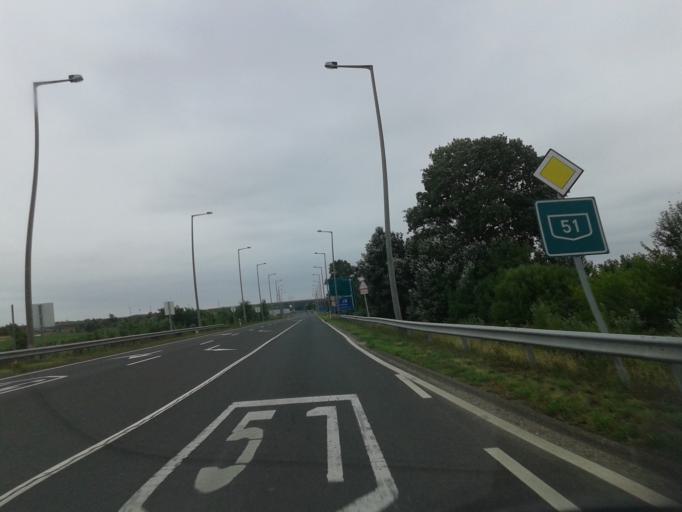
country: HU
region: Bacs-Kiskun
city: Dunavecse
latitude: 46.9016
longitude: 18.9887
